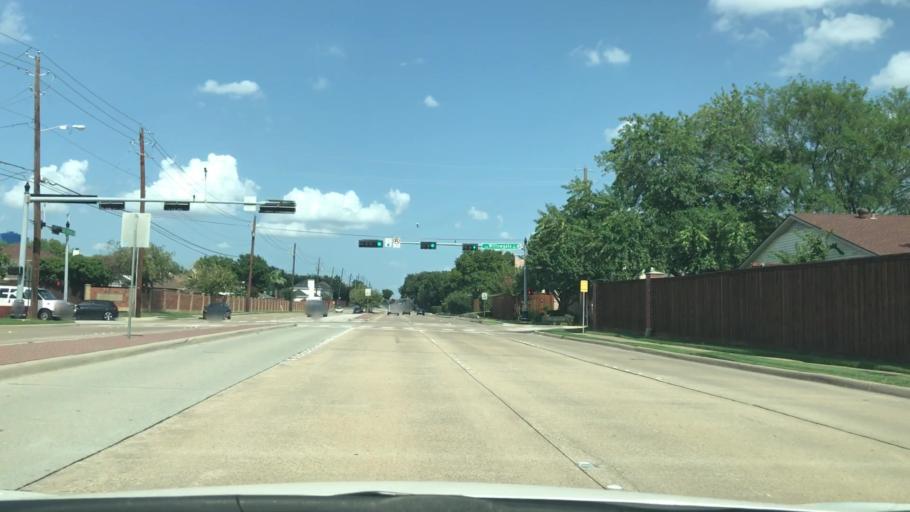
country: US
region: Texas
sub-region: Dallas County
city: Carrollton
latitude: 32.9702
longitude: -96.8649
